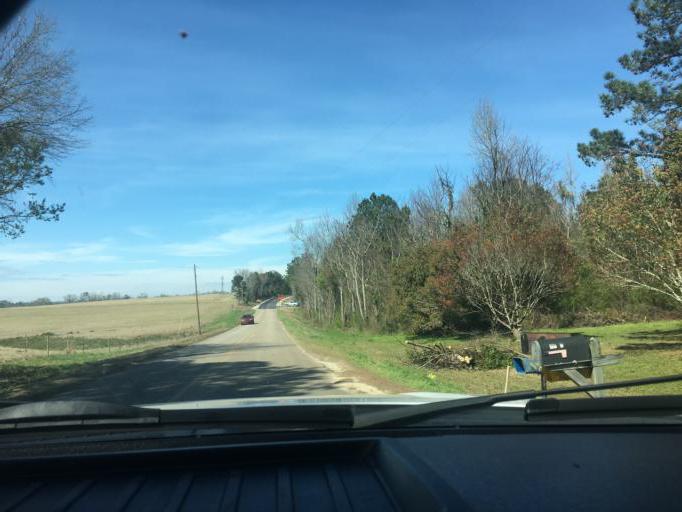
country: US
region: Alabama
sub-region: Lee County
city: Auburn
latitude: 32.4704
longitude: -85.4030
